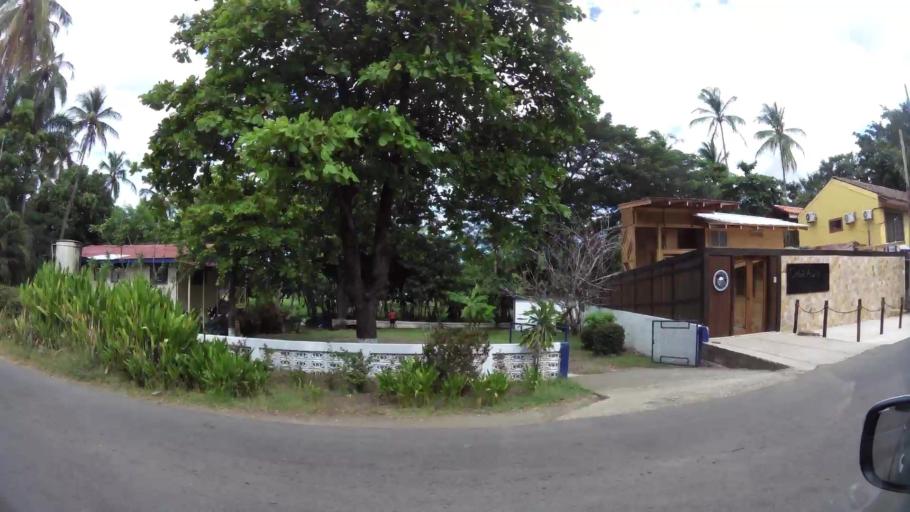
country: CR
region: Guanacaste
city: Santa Cruz
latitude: 10.3040
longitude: -85.8383
